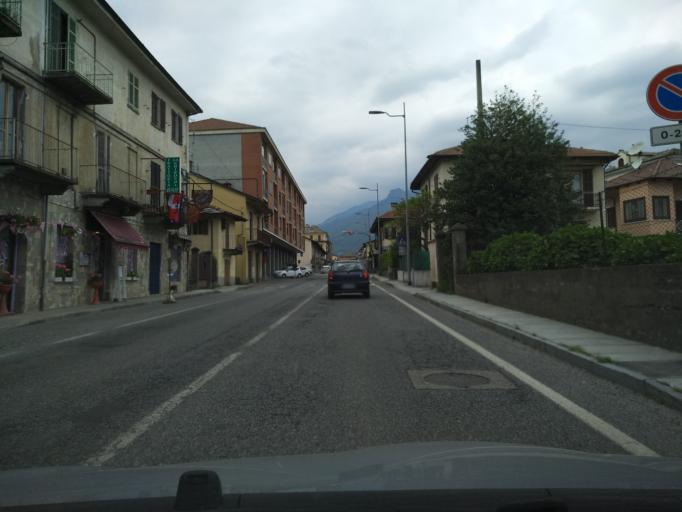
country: IT
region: Piedmont
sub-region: Provincia di Torino
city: Airali
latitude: 44.8132
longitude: 7.2514
